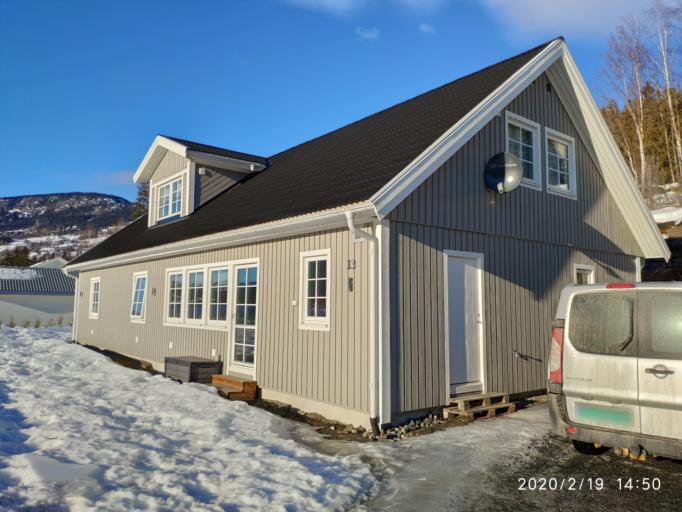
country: NO
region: Oppland
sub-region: Oyer
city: Tretten
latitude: 61.2695
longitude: 10.4082
